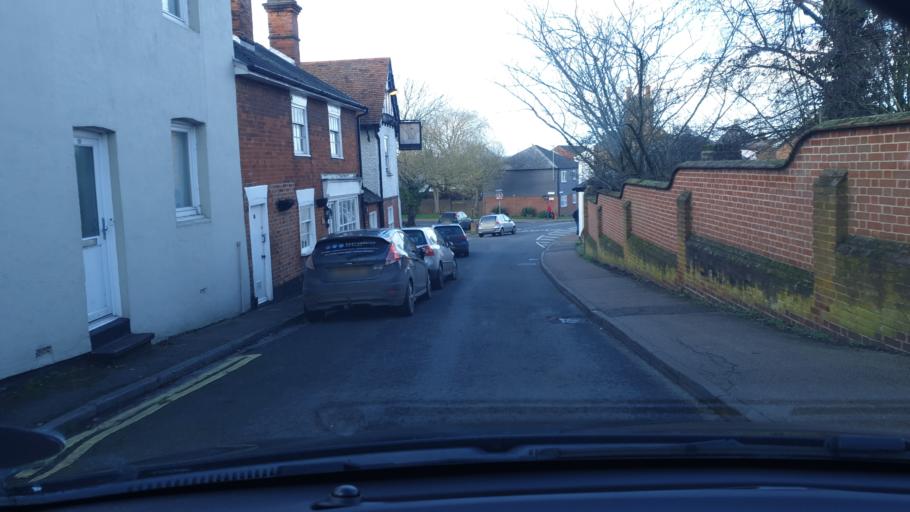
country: GB
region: England
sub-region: Essex
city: Manningtree
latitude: 51.9439
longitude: 1.0630
